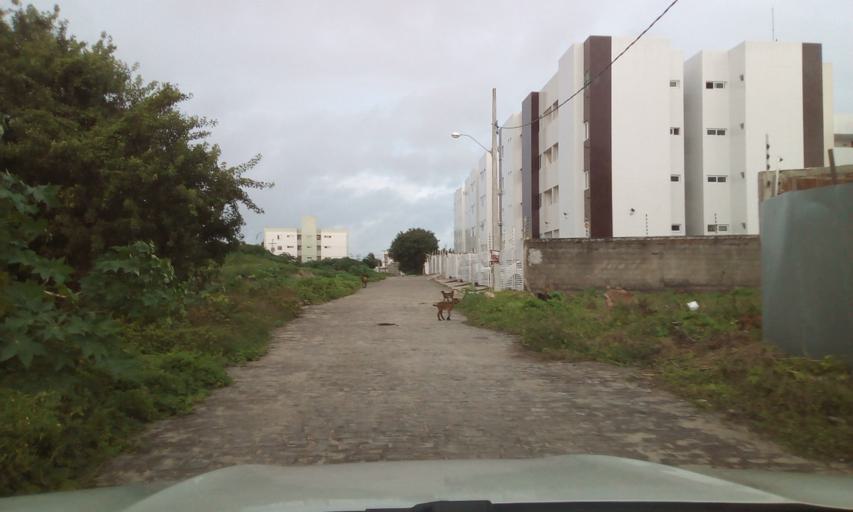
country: BR
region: Paraiba
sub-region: Joao Pessoa
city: Joao Pessoa
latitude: -7.1634
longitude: -34.8555
